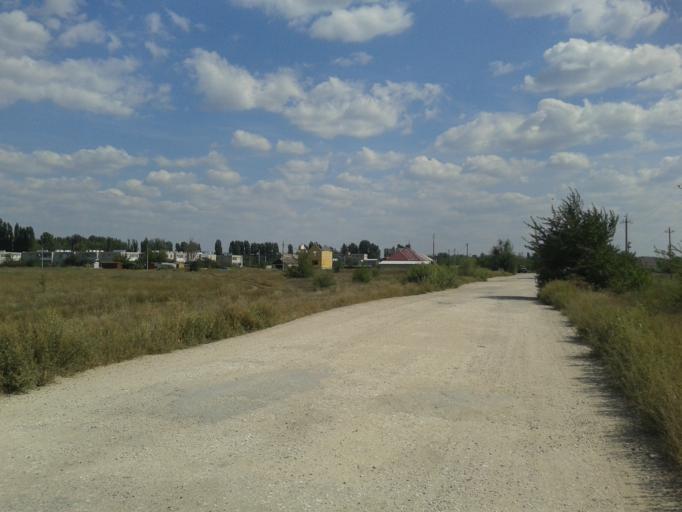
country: RU
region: Volgograd
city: Frolovo
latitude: 49.7458
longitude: 43.6456
